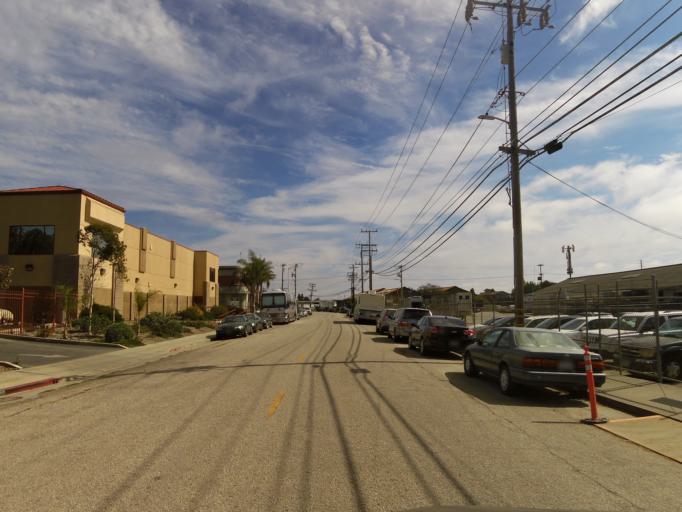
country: US
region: California
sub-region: Santa Cruz County
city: Santa Cruz
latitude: 36.9598
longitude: -122.0541
